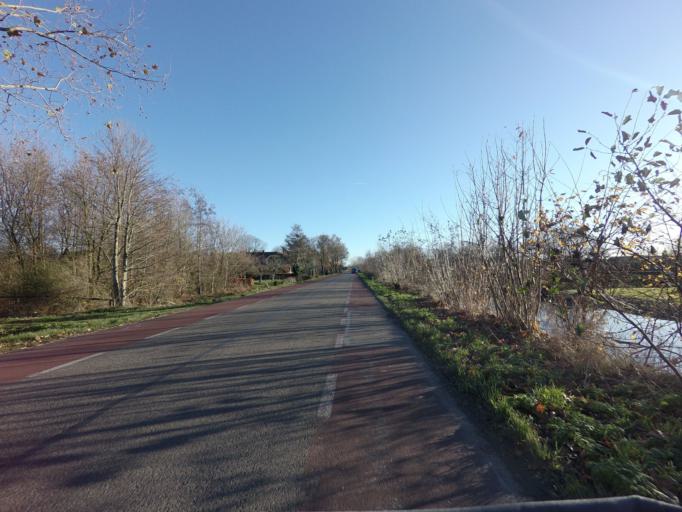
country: NL
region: Utrecht
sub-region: Stichtse Vecht
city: Vreeland
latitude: 52.2441
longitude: 4.9927
